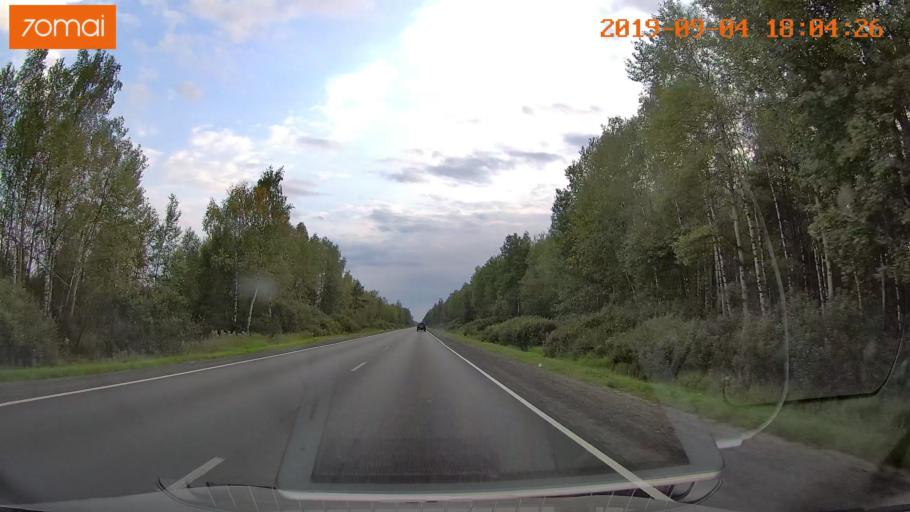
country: RU
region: Moskovskaya
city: Il'inskiy Pogost
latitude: 55.4522
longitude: 38.8391
